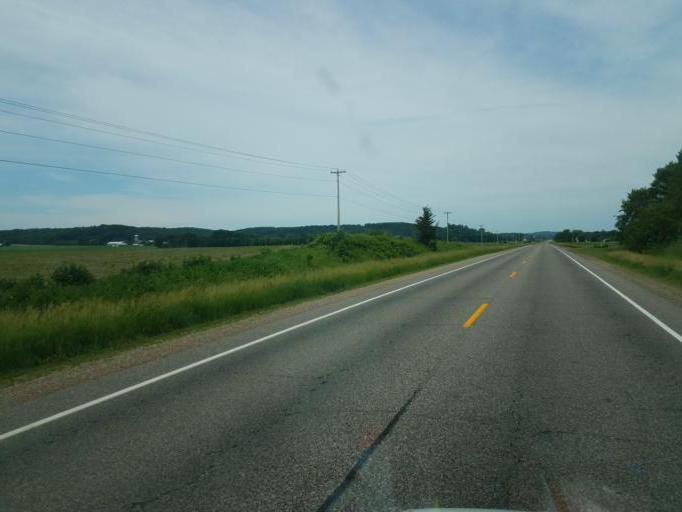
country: US
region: Wisconsin
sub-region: Juneau County
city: Mauston
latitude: 43.7891
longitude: -90.1007
